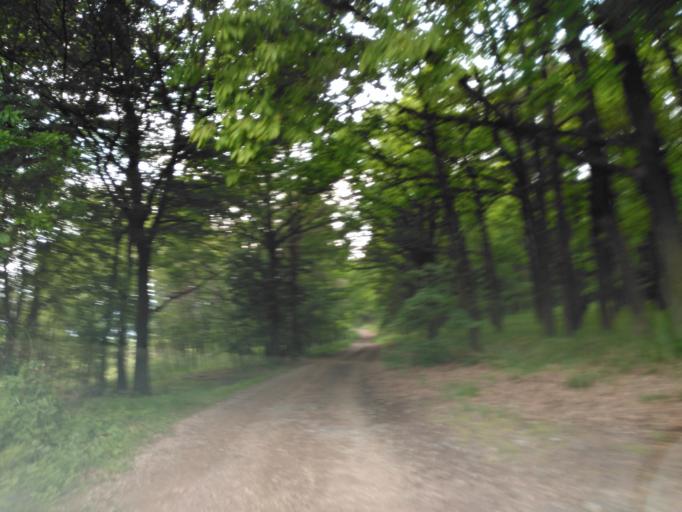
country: CZ
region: Plzensky
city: Zbiroh
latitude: 49.8578
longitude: 13.7437
